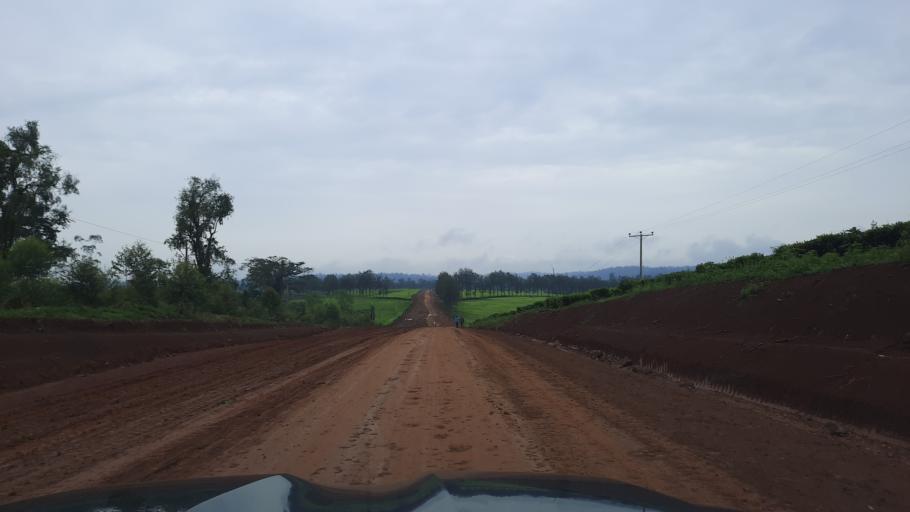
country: ET
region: Oromiya
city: Gore
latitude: 7.8467
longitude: 35.4766
